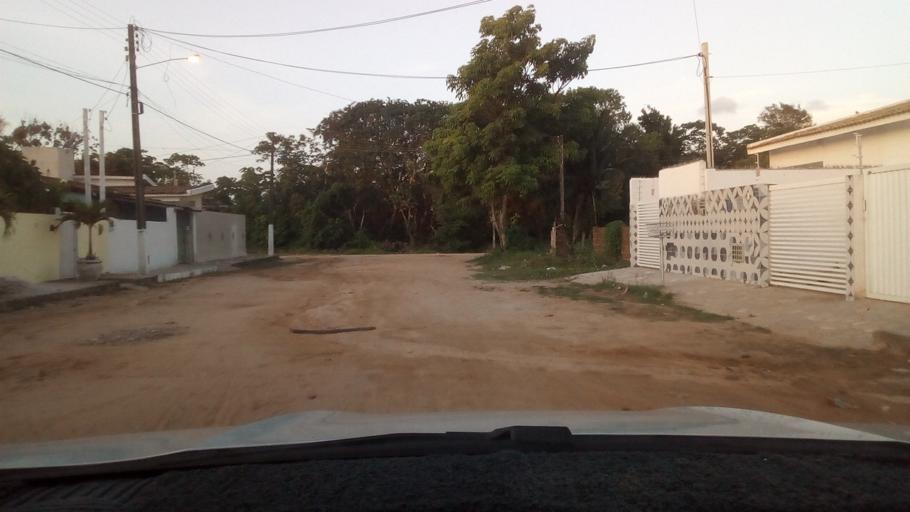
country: BR
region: Paraiba
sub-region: Bayeux
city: Bayeux
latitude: -7.1718
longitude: -34.9295
